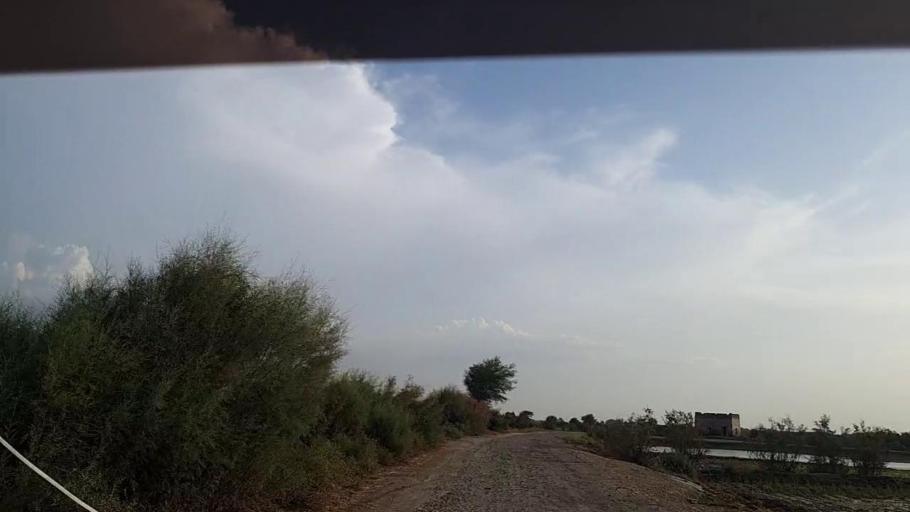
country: PK
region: Sindh
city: Khanpur
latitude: 27.8022
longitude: 69.3135
